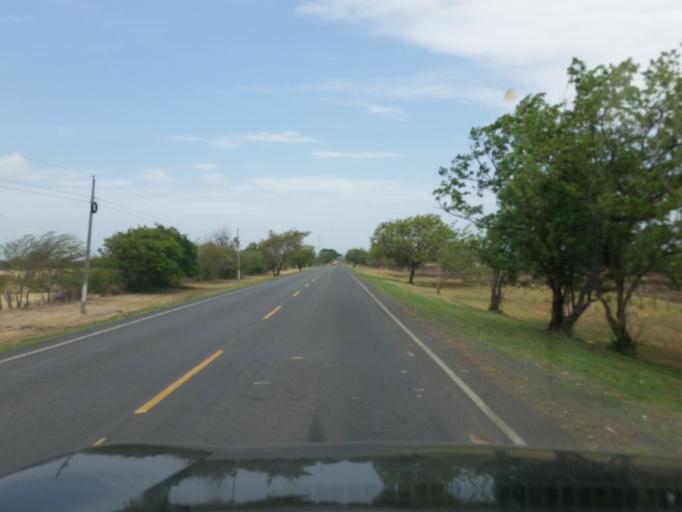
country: NI
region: Granada
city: Nandaime
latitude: 11.6706
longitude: -85.9785
